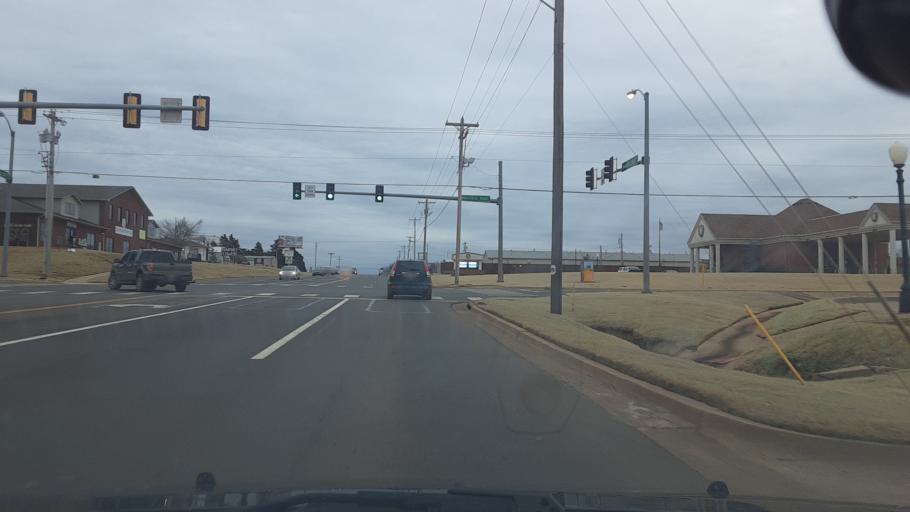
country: US
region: Oklahoma
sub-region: Logan County
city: Guthrie
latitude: 35.8566
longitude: -97.4255
